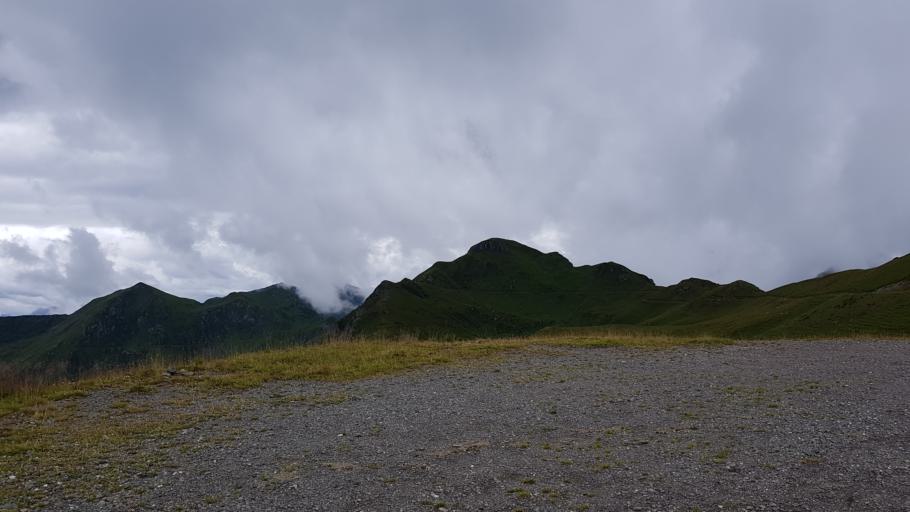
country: IT
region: Friuli Venezia Giulia
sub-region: Provincia di Udine
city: Cercivento
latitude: 46.5617
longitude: 12.9689
